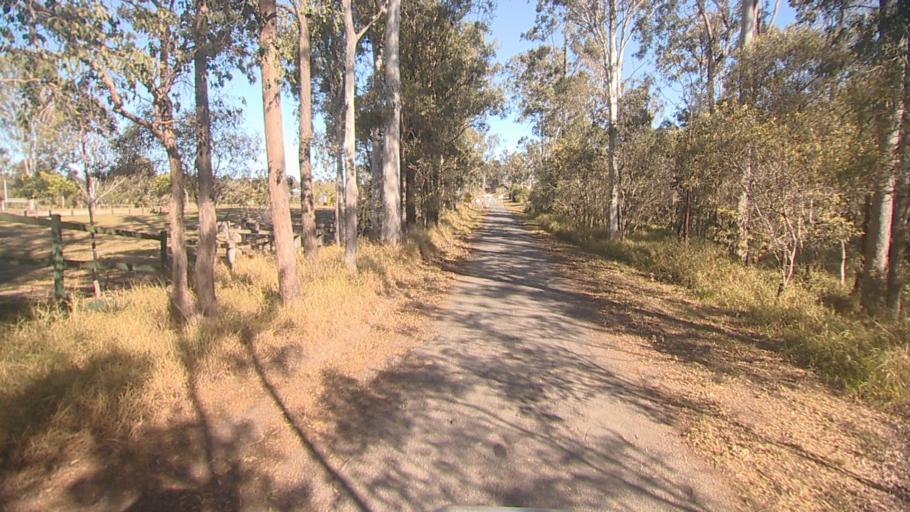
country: AU
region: Queensland
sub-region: Ipswich
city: Springfield Lakes
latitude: -27.7391
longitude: 152.9218
